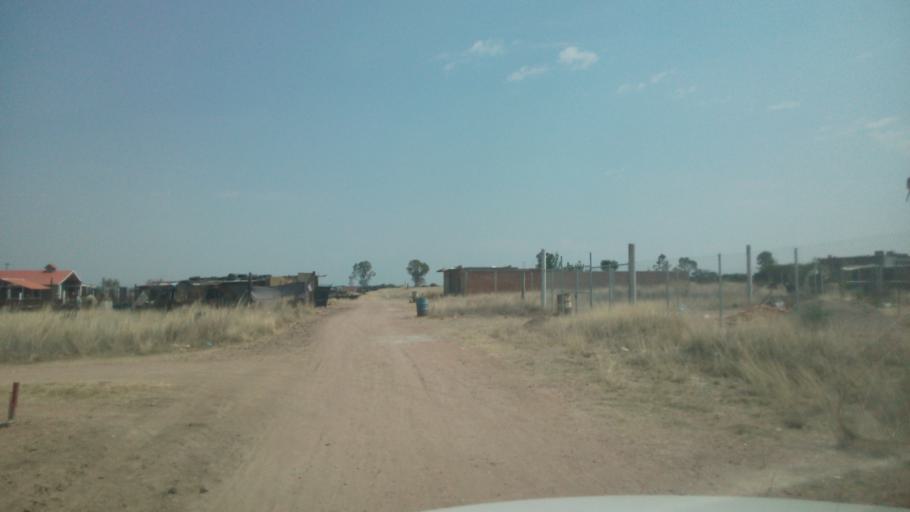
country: MX
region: Aguascalientes
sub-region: Aguascalientes
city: Villa Licenciado Jesus Teran (Calvillito)
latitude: 21.8450
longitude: -102.1642
